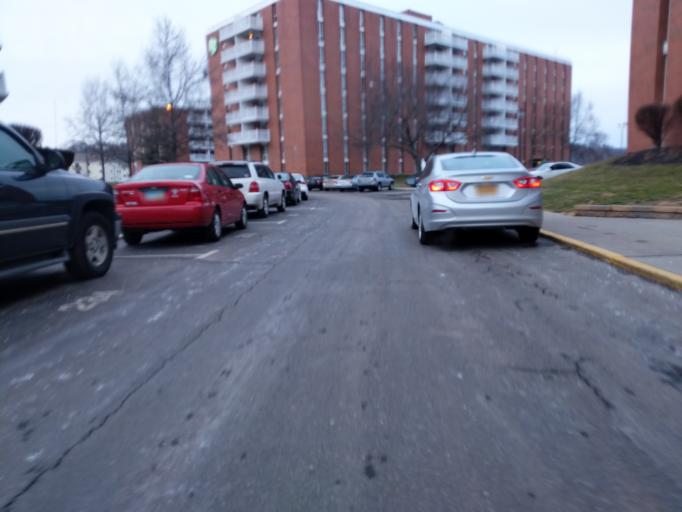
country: US
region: Ohio
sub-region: Athens County
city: Athens
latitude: 39.3258
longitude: -82.0931
